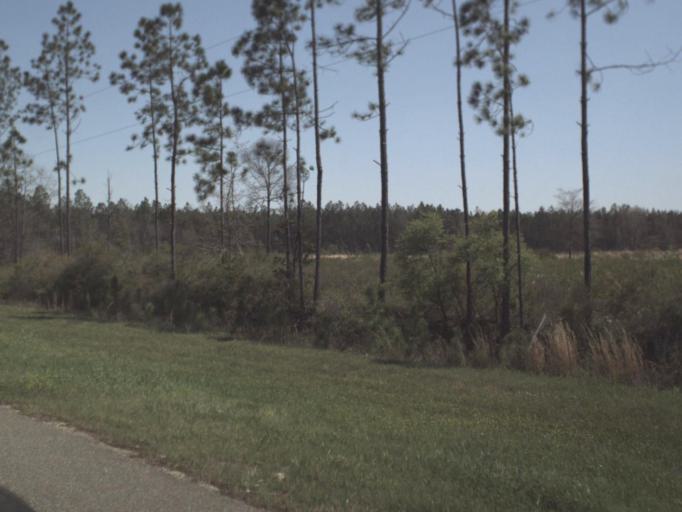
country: US
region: Florida
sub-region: Calhoun County
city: Blountstown
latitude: 30.4257
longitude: -85.1277
